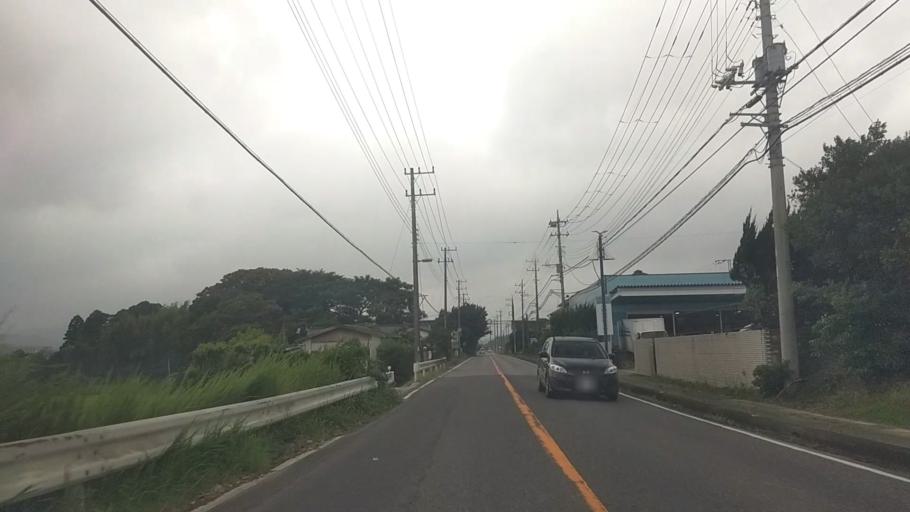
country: JP
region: Chiba
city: Kawaguchi
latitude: 35.1225
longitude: 140.0645
